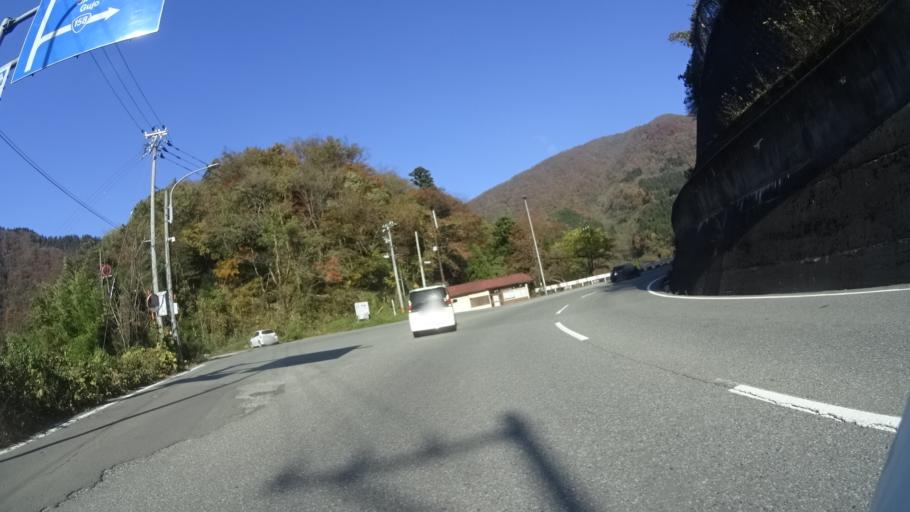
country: JP
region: Fukui
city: Ono
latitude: 35.9676
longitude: 136.5928
